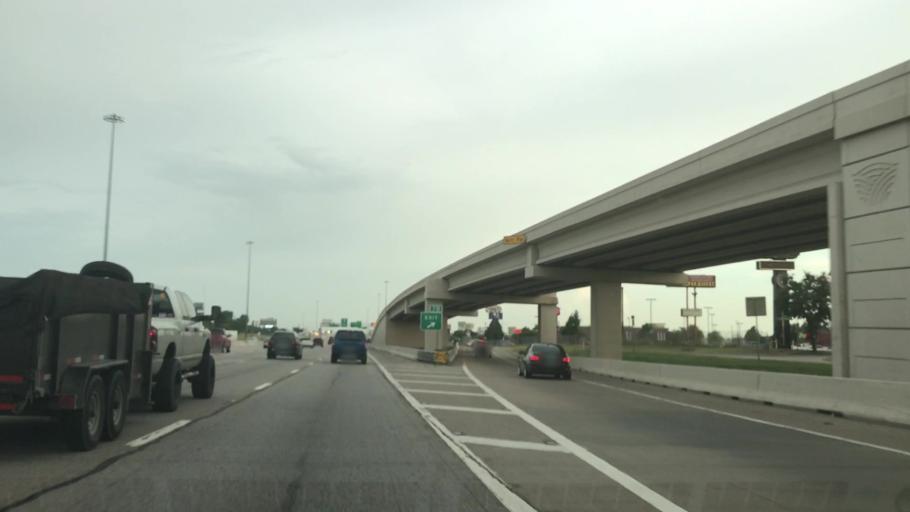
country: US
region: Texas
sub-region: Dallas County
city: Mesquite
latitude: 32.8176
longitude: -96.6290
